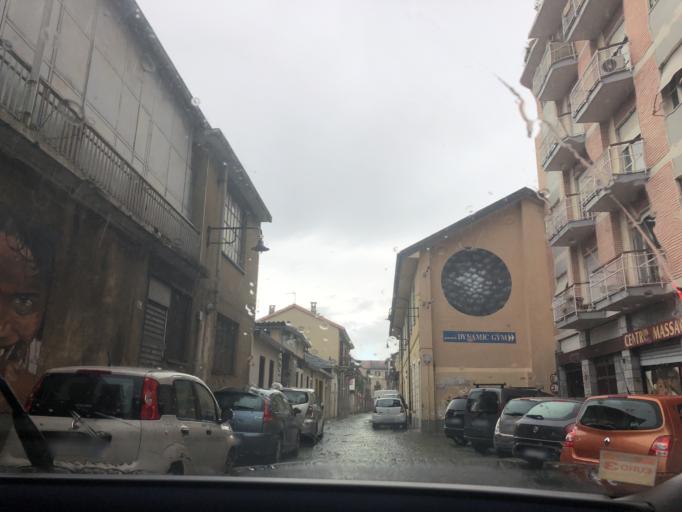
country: IT
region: Piedmont
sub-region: Provincia di Torino
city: Turin
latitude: 45.0823
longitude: 7.6522
